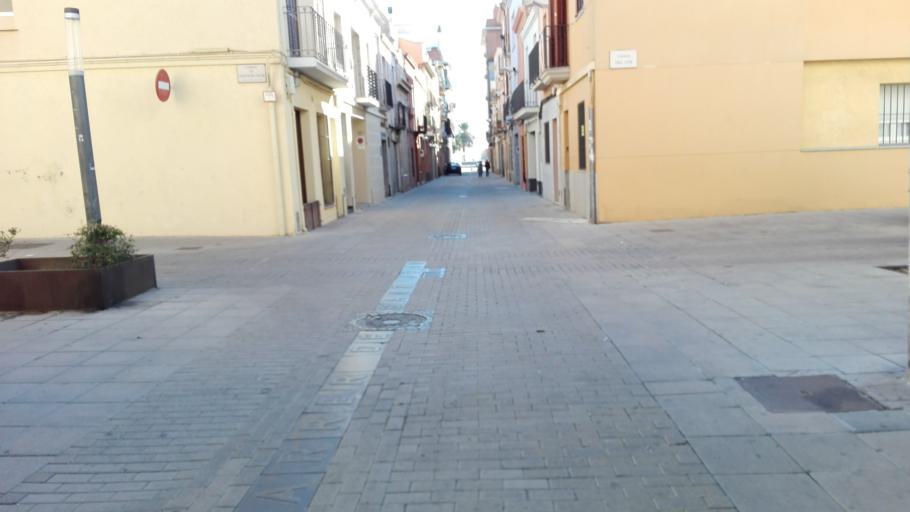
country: ES
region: Catalonia
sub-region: Provincia de Barcelona
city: Mataro
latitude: 41.5376
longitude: 2.4485
